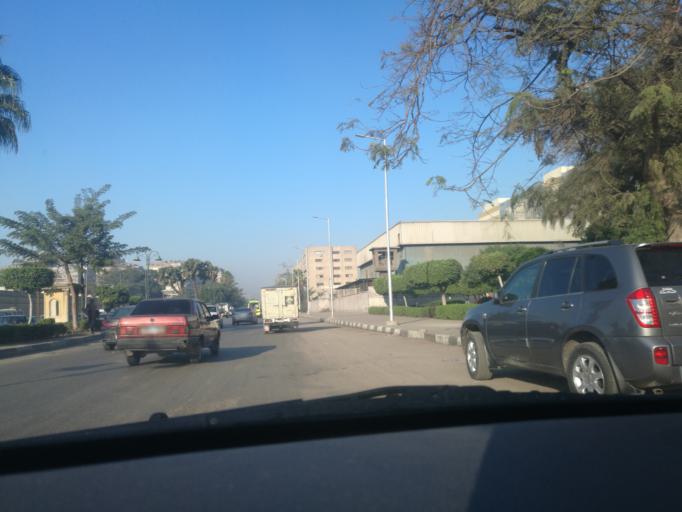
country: EG
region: Muhafazat al Qahirah
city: Cairo
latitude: 30.1020
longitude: 31.3055
